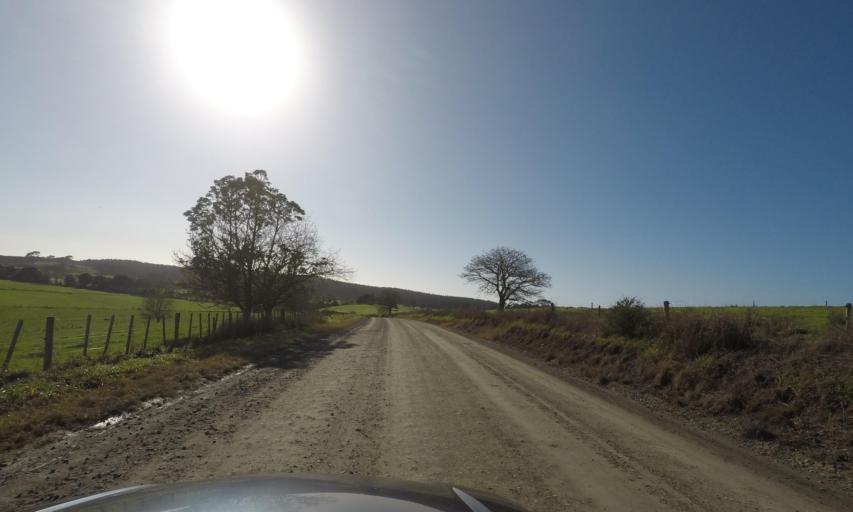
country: NZ
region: Auckland
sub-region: Auckland
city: Wellsford
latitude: -36.1602
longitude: 174.6105
